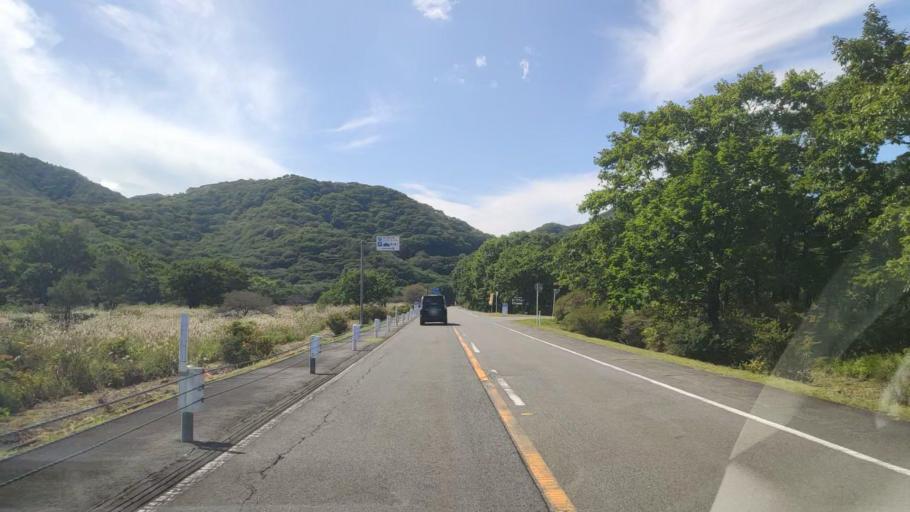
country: JP
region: Gunma
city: Shibukawa
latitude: 36.4721
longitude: 138.8844
